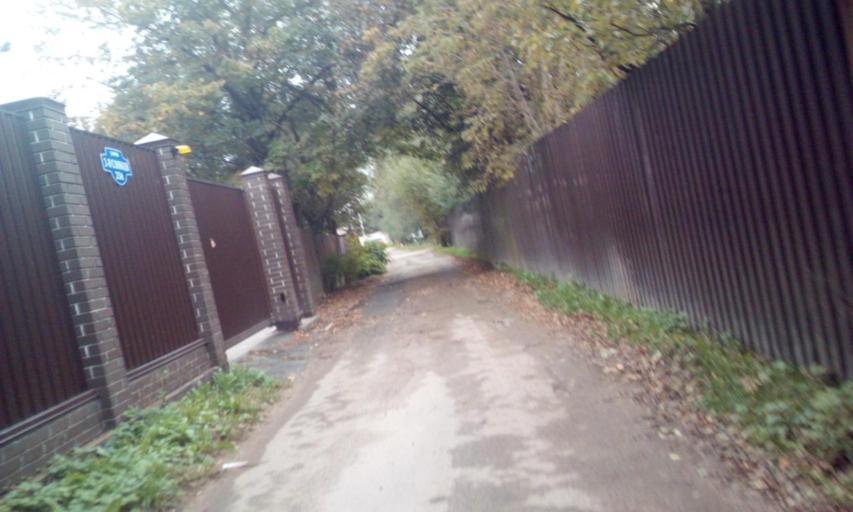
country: RU
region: Moskovskaya
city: Zhavoronki
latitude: 55.6450
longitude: 37.1083
